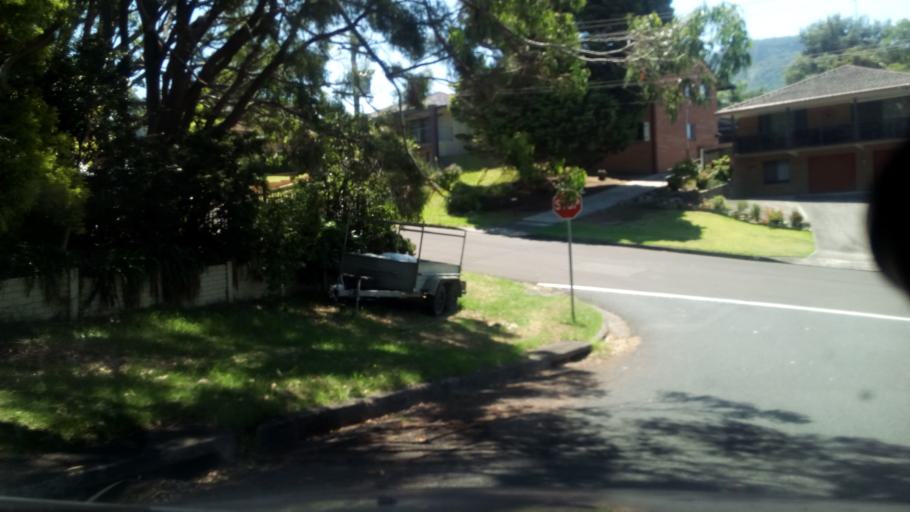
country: AU
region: New South Wales
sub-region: Wollongong
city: Mount Keira
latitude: -34.4237
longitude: 150.8576
